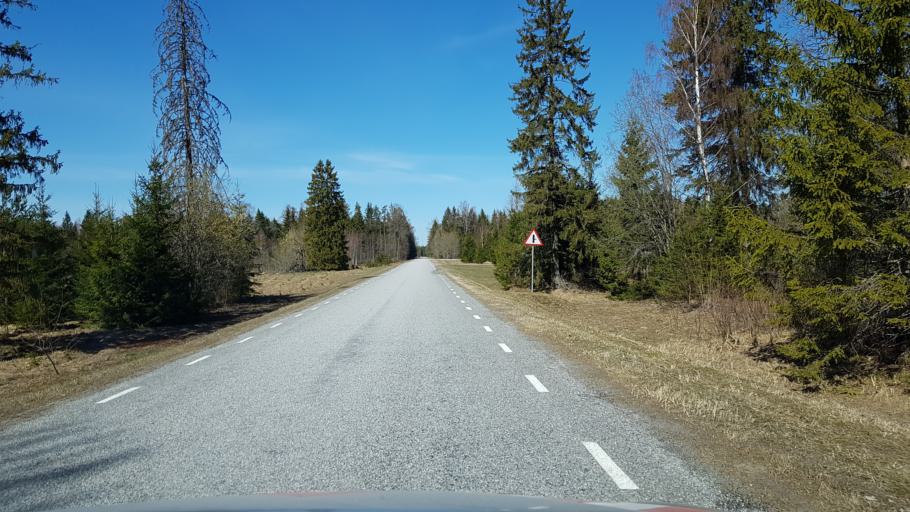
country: EE
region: Laeaene-Virumaa
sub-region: Vinni vald
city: Vinni
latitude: 59.1648
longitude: 26.5106
